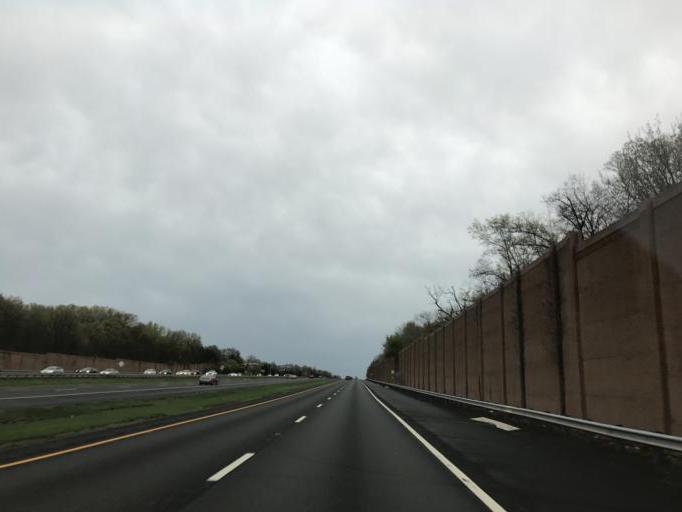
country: US
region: New Jersey
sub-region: Somerset County
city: Bridgewater
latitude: 40.6162
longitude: -74.6350
